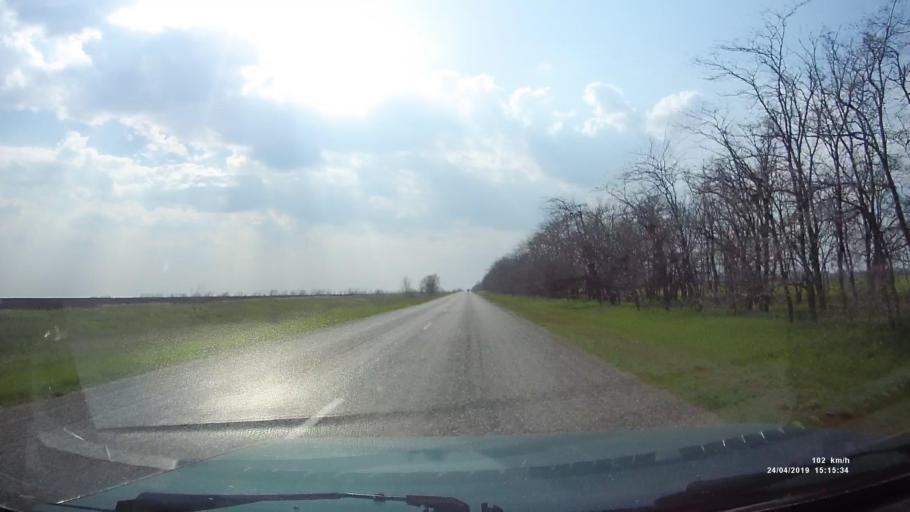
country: RU
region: Rostov
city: Remontnoye
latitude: 46.5465
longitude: 43.2323
